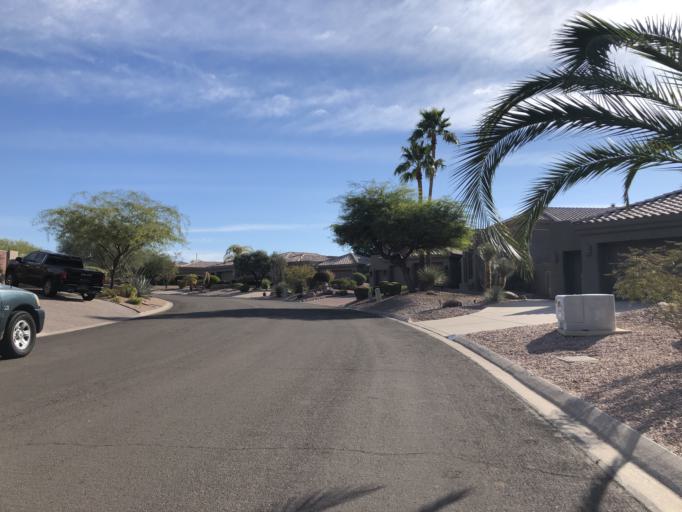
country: US
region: Arizona
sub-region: Maricopa County
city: Fountain Hills
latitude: 33.4890
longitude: -111.6877
